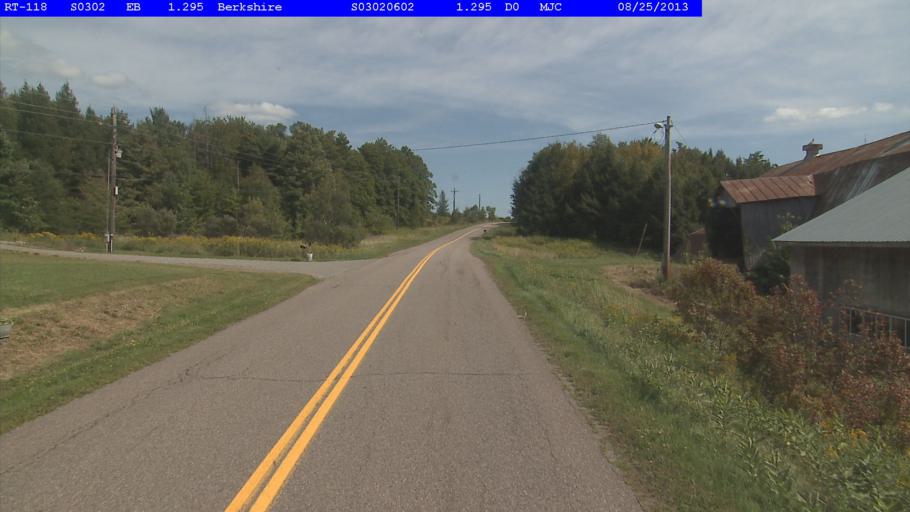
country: US
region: Vermont
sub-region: Franklin County
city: Enosburg Falls
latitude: 44.9812
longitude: -72.7907
